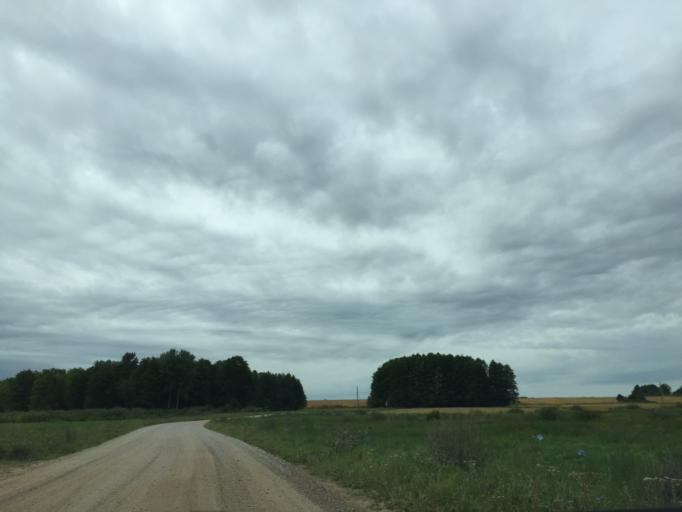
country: LV
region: Dobeles Rajons
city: Dobele
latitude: 56.7813
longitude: 23.2431
